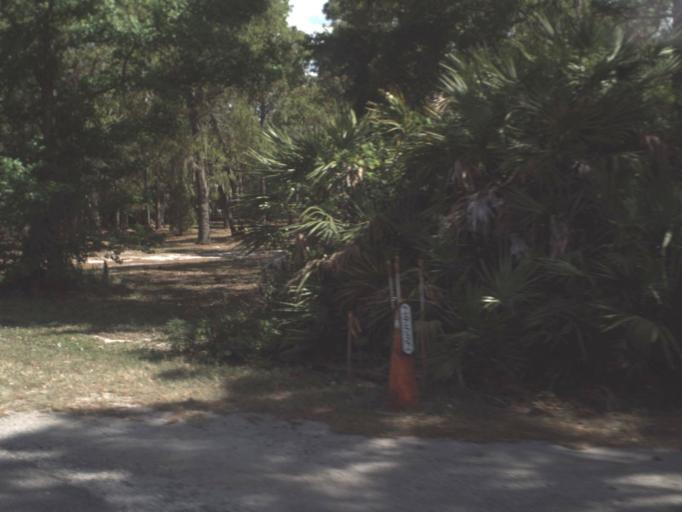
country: US
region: Florida
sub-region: Lake County
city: Mount Plymouth
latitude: 28.8136
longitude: -81.4682
